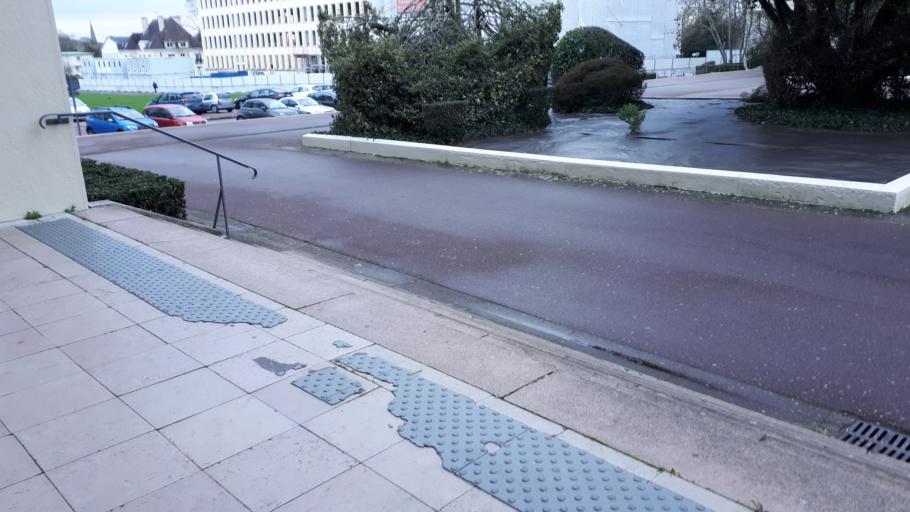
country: FR
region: Lower Normandy
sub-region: Departement du Calvados
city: Caen
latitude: 49.1904
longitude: -0.3640
